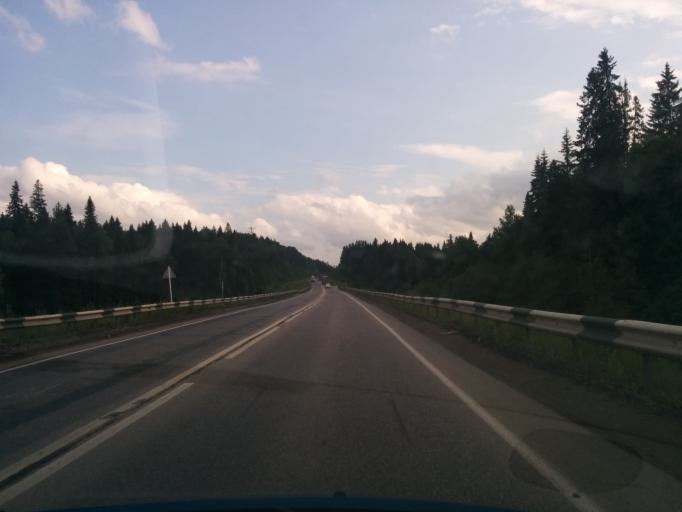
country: RU
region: Perm
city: Novyye Lyady
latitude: 58.0879
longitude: 56.4284
